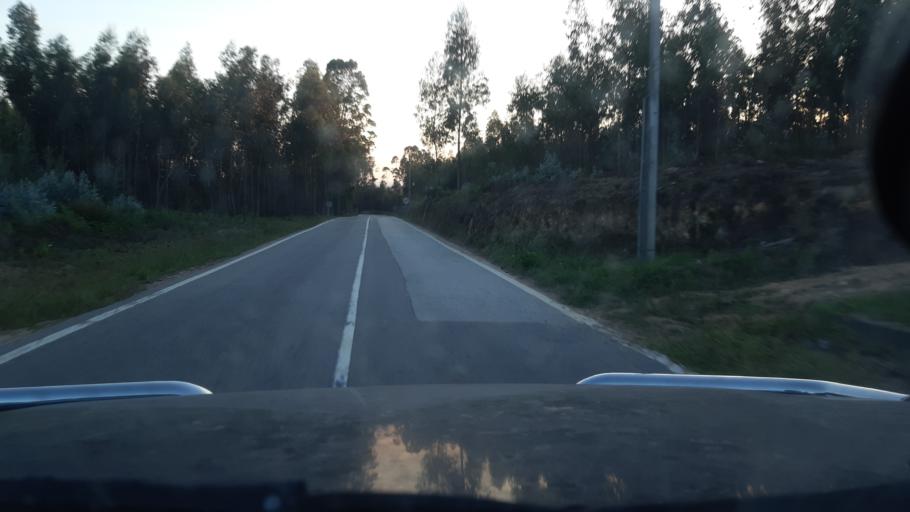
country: PT
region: Aveiro
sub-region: Agueda
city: Aguada de Cima
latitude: 40.5649
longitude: -8.3732
